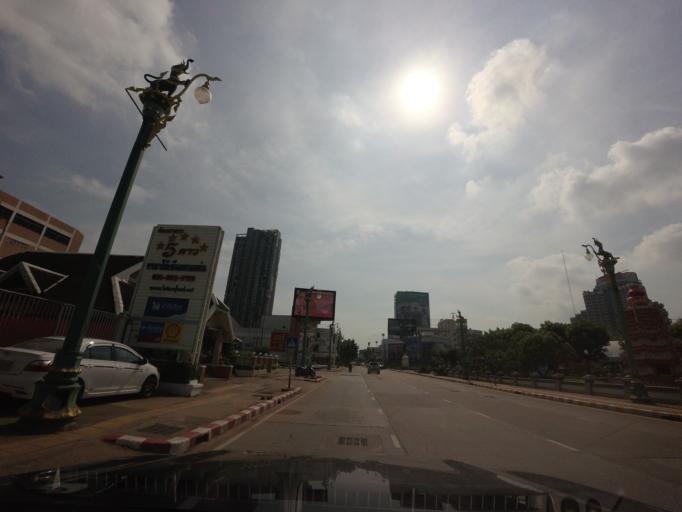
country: TH
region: Khon Kaen
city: Khon Kaen
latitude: 16.4314
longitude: 102.8283
